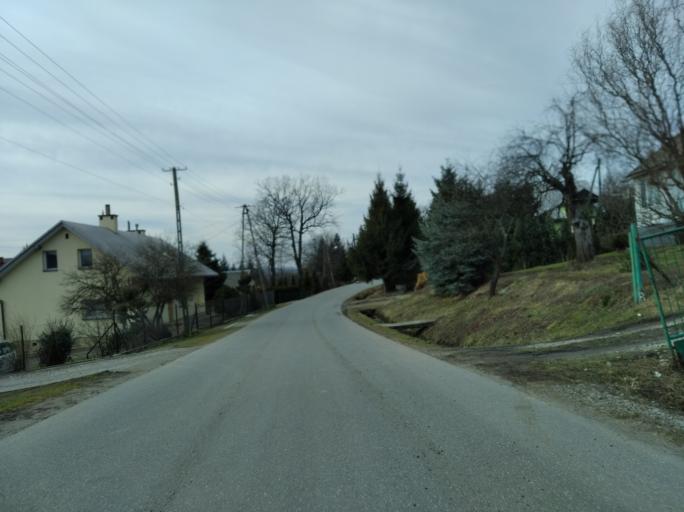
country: PL
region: Subcarpathian Voivodeship
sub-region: Powiat brzozowski
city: Gorki
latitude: 49.6484
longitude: 22.0373
